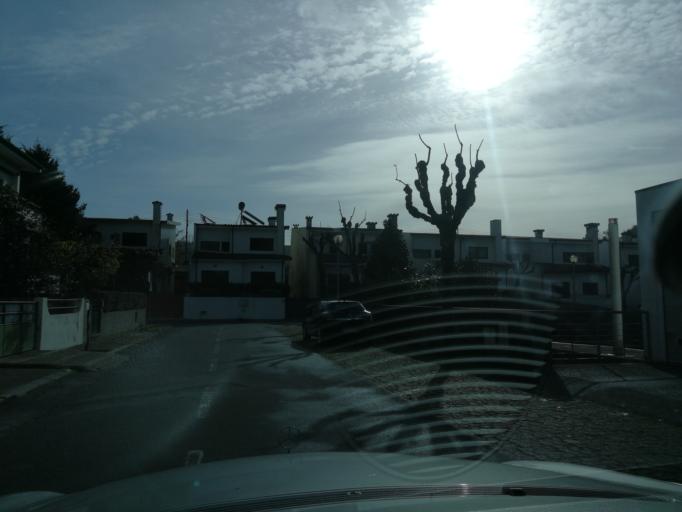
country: PT
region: Braga
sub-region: Braga
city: Braga
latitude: 41.5355
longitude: -8.4130
